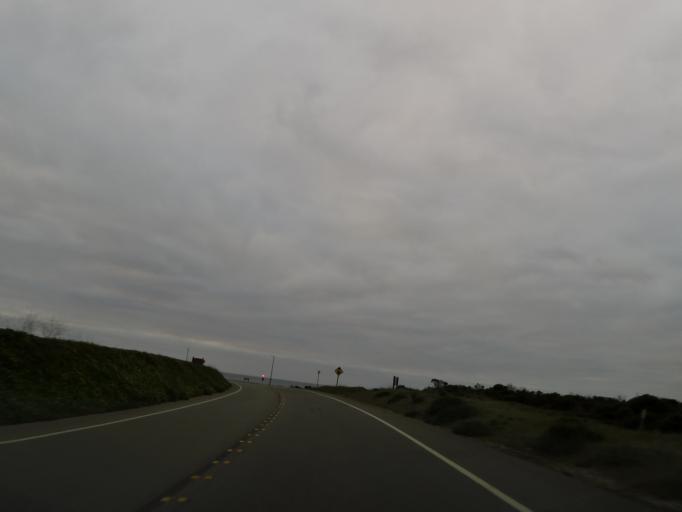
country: US
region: California
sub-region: San Mateo County
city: Half Moon Bay
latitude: 37.2595
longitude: -122.4109
